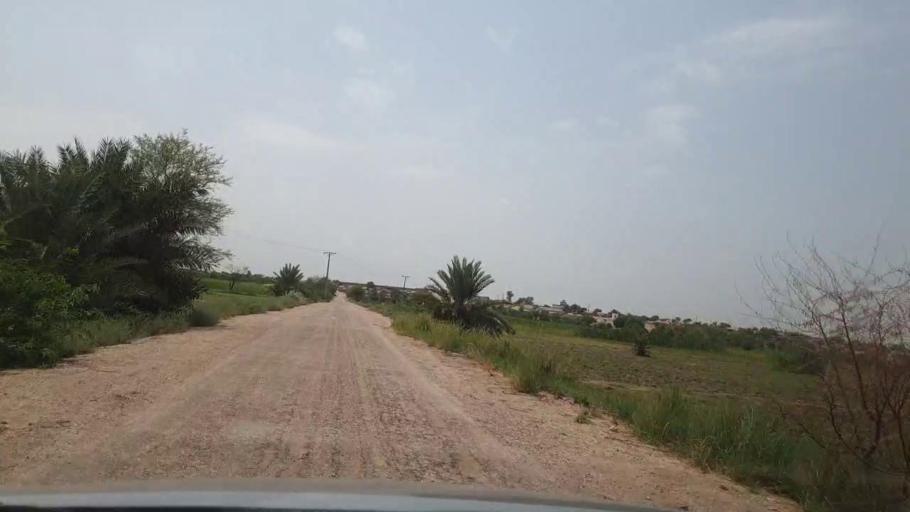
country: PK
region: Sindh
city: Pano Aqil
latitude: 27.5905
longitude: 69.1985
